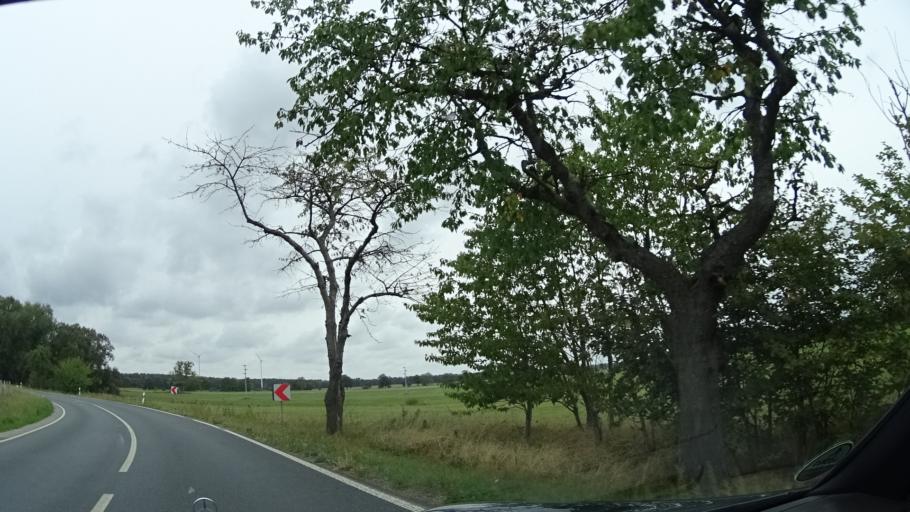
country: DE
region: Brandenburg
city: Dabergotz
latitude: 52.9457
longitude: 12.7107
